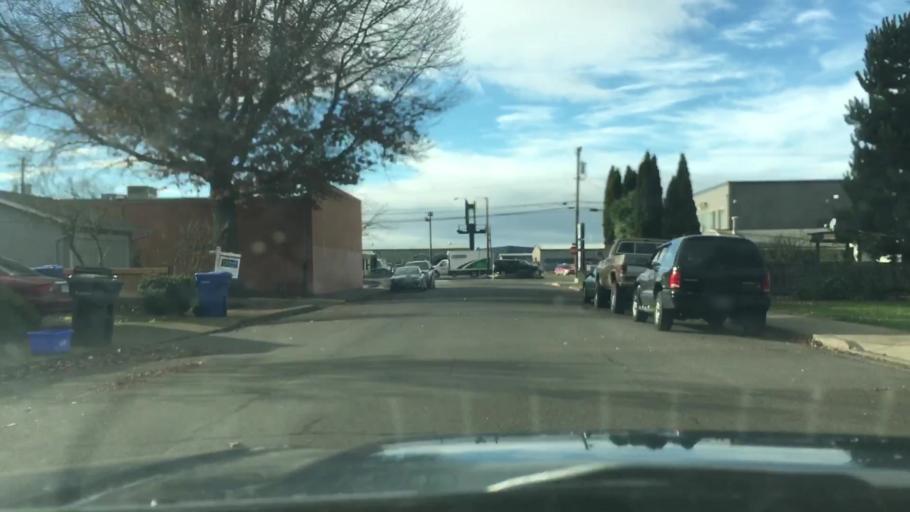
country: US
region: Oregon
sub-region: Lane County
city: Eugene
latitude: 44.0493
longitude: -123.1219
